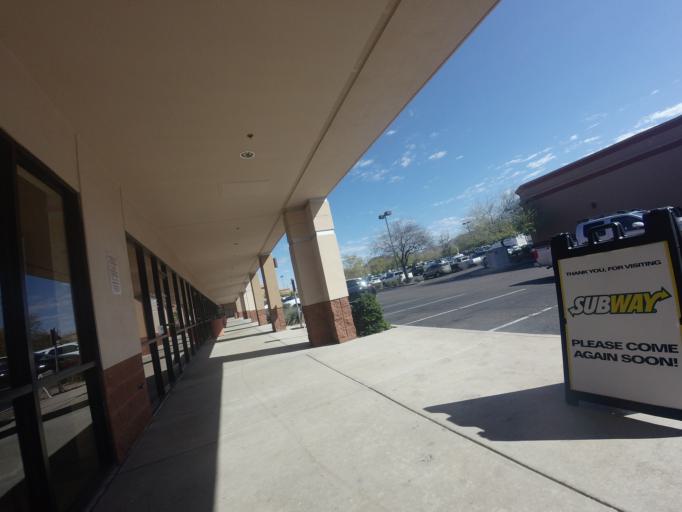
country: US
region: Arizona
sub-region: Maricopa County
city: Mesa
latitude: 33.4668
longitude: -111.6854
